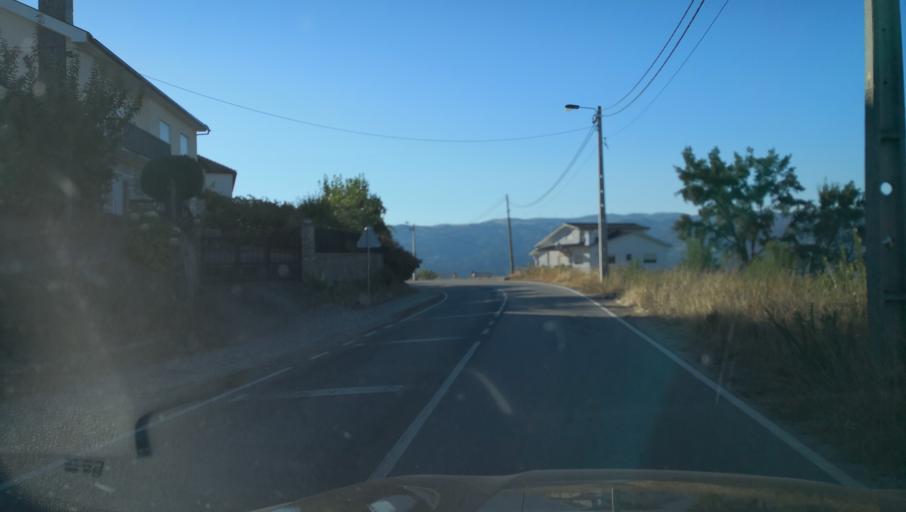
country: PT
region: Vila Real
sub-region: Vila Real
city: Vila Real
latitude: 41.2820
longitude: -7.7237
